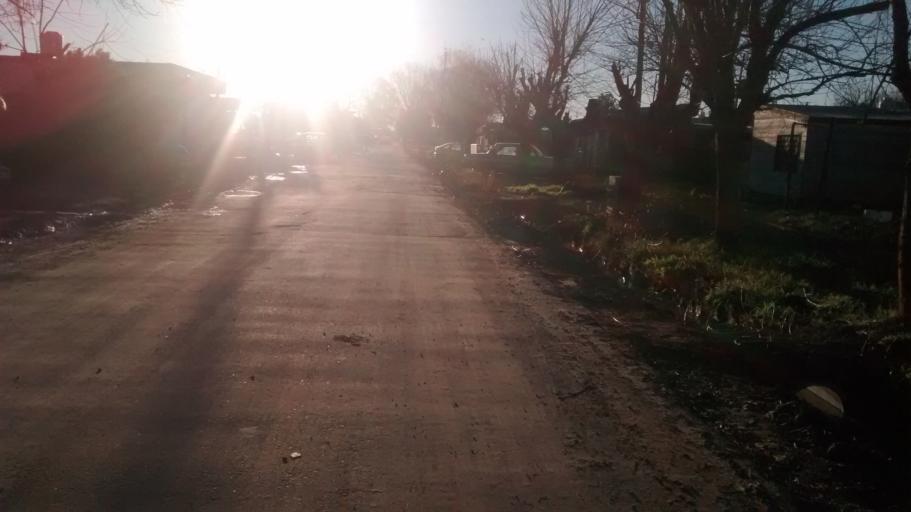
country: AR
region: Buenos Aires
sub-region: Partido de La Plata
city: La Plata
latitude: -34.9635
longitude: -57.9390
